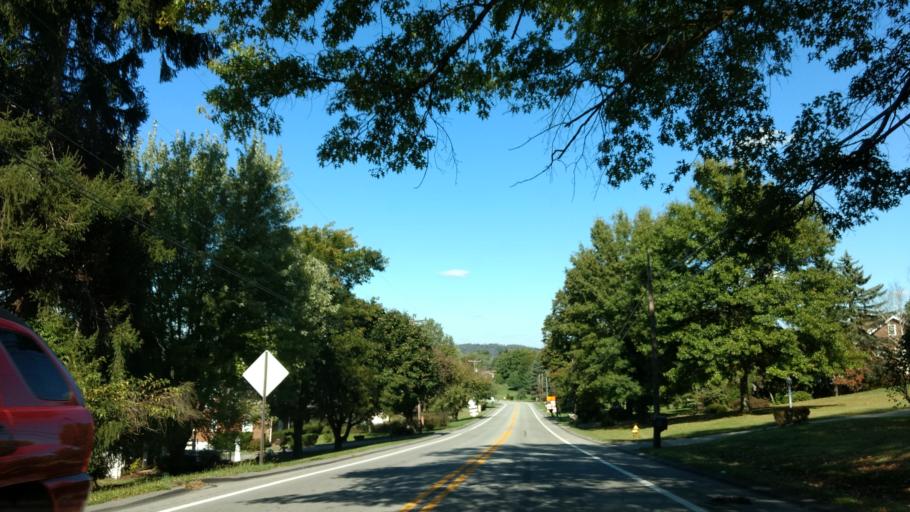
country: US
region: Pennsylvania
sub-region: Washington County
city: Wickerham Manor-Fisher
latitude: 40.1743
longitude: -79.9141
